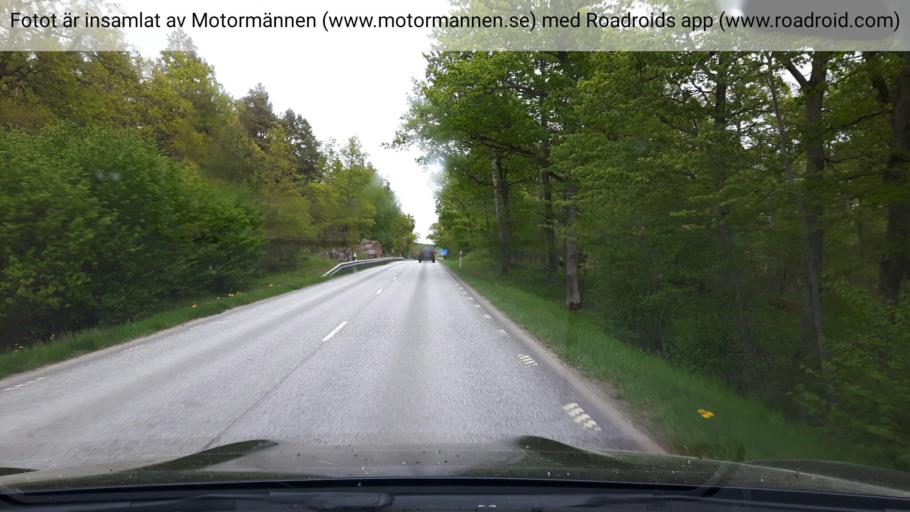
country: SE
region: Stockholm
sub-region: Varmdo Kommun
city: Hemmesta
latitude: 59.5554
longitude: 18.5508
